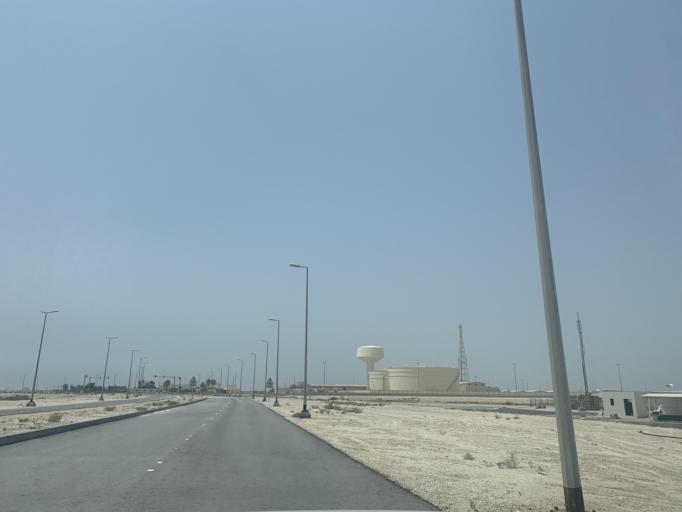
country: BH
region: Central Governorate
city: Dar Kulayb
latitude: 25.8417
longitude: 50.5883
